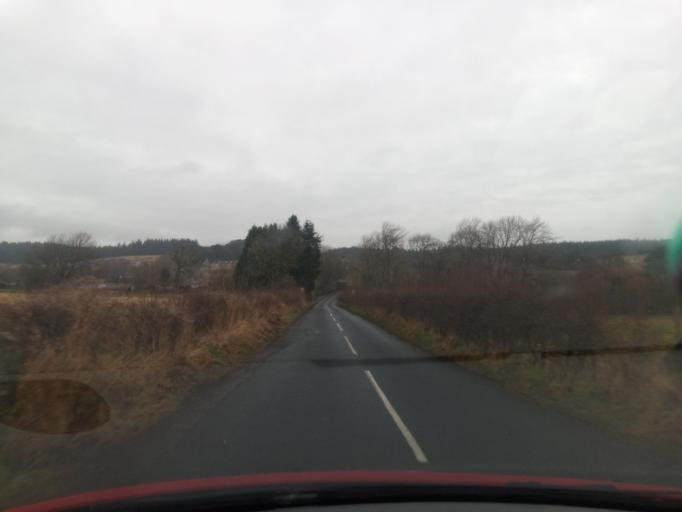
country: GB
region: England
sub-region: Northumberland
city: Rochester
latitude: 55.1787
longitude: -2.4366
